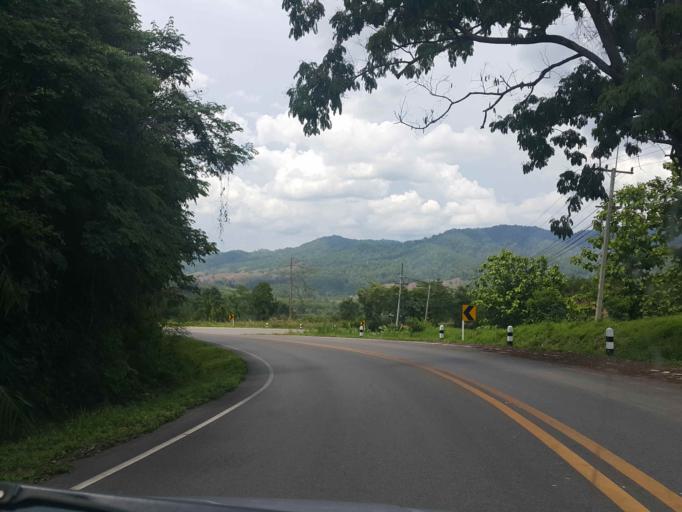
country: TH
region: Nan
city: Ban Luang
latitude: 18.8616
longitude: 100.4573
